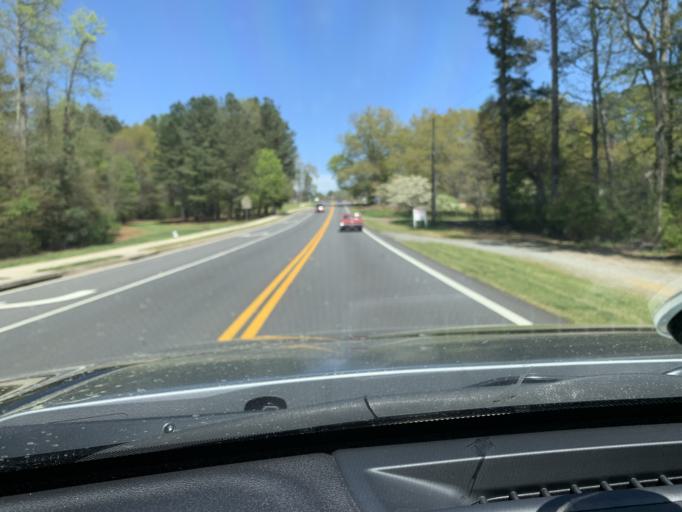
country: US
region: Georgia
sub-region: Forsyth County
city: Cumming
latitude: 34.1789
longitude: -84.2209
